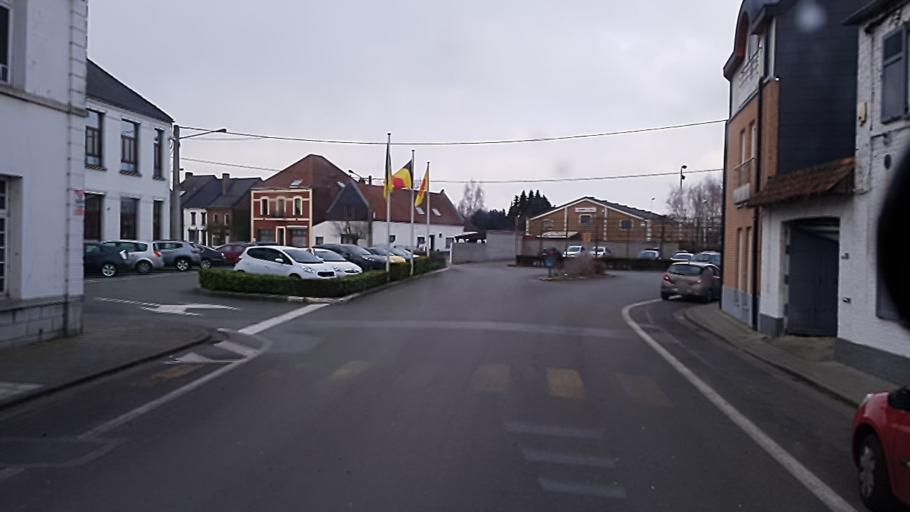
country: BE
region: Wallonia
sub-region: Province du Hainaut
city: Saint-Ghislain
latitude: 50.4675
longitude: 3.8076
